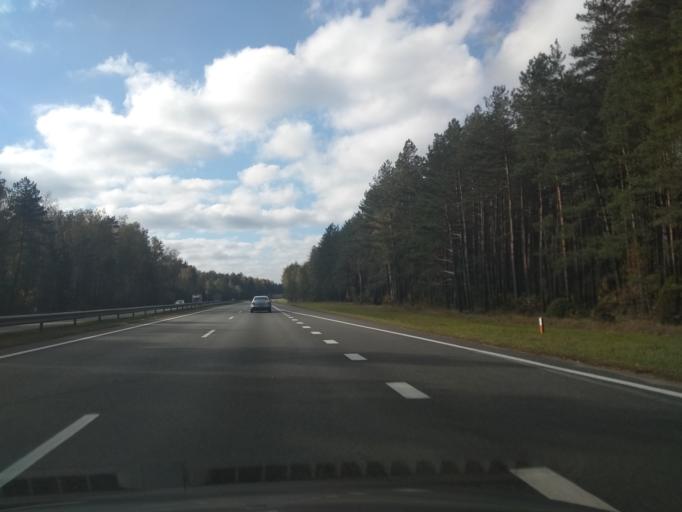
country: BY
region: Minsk
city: Enyerhyetykaw
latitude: 53.5547
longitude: 26.9679
